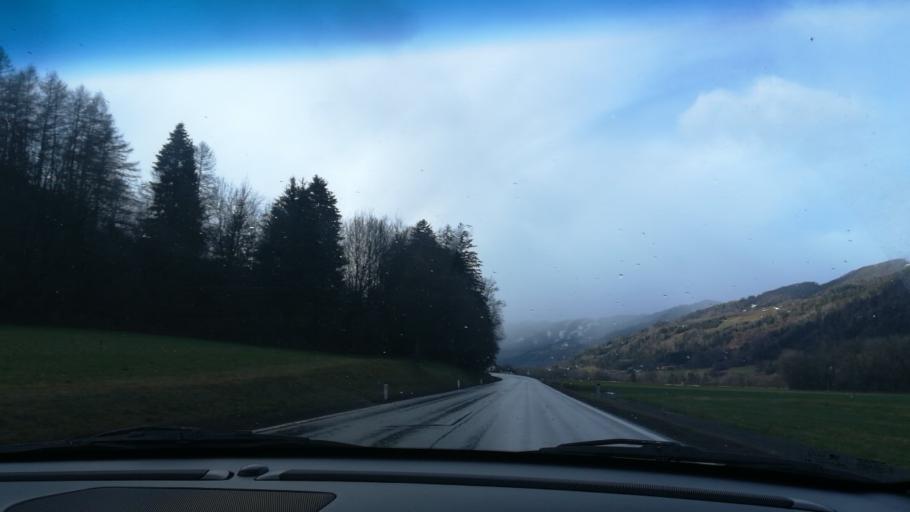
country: AT
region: Styria
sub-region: Politischer Bezirk Murtal
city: Poels
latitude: 47.2034
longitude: 14.5558
